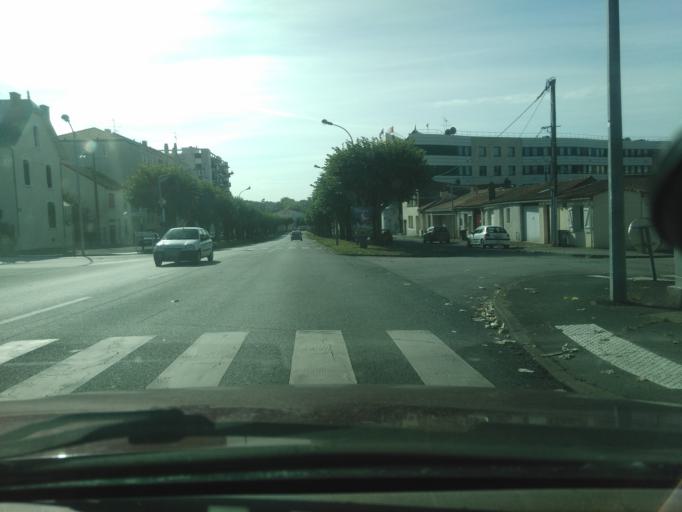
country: FR
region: Pays de la Loire
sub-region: Departement de la Vendee
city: La Roche-sur-Yon
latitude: 46.6750
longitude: -1.4236
